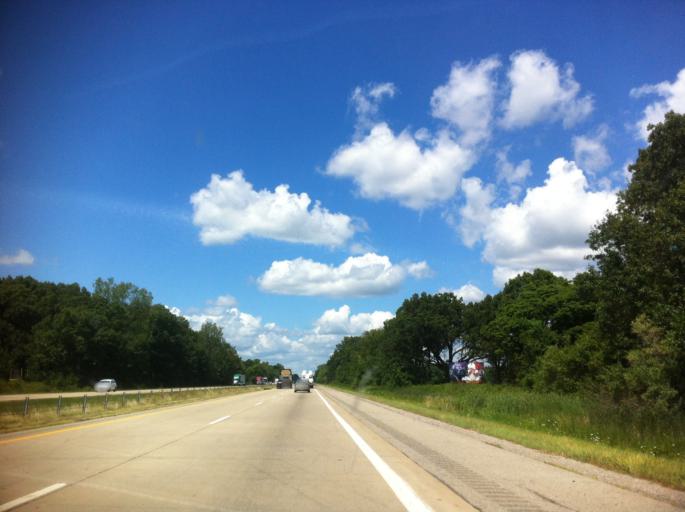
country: US
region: Michigan
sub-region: Monroe County
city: Petersburg
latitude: 41.8718
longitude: -83.6610
